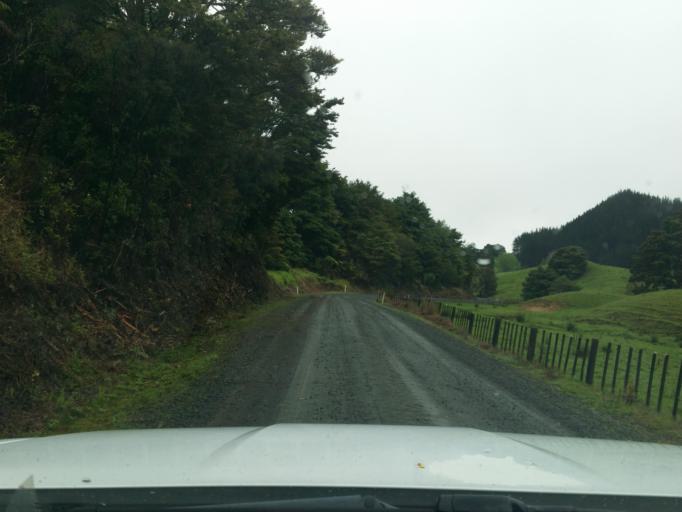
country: NZ
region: Northland
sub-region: Kaipara District
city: Dargaville
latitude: -35.7641
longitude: 173.9377
